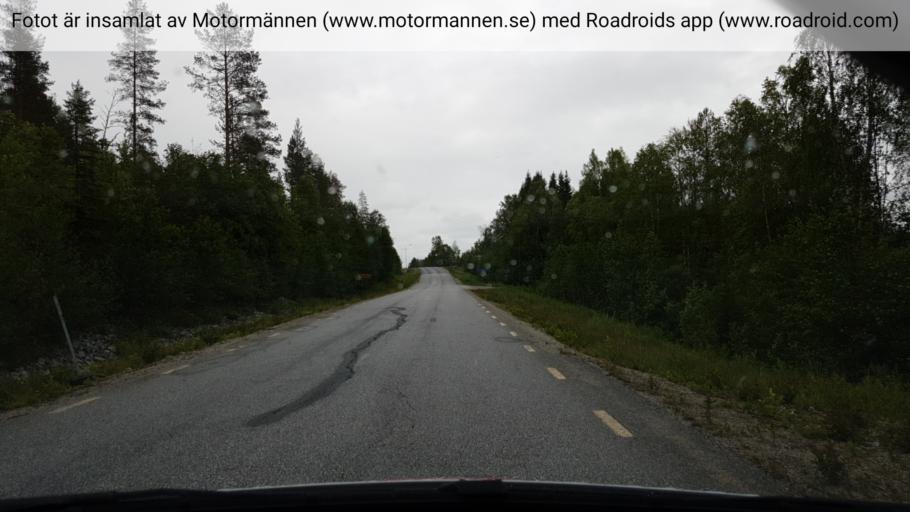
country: SE
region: Vaesterbotten
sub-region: Bjurholms Kommun
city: Bjurholm
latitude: 64.0310
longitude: 19.3312
